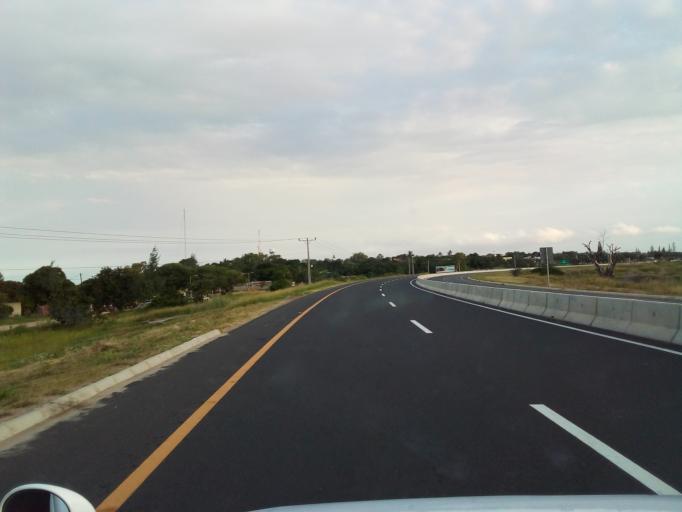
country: MZ
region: Maputo City
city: Maputo
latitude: -25.9999
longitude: 32.5578
